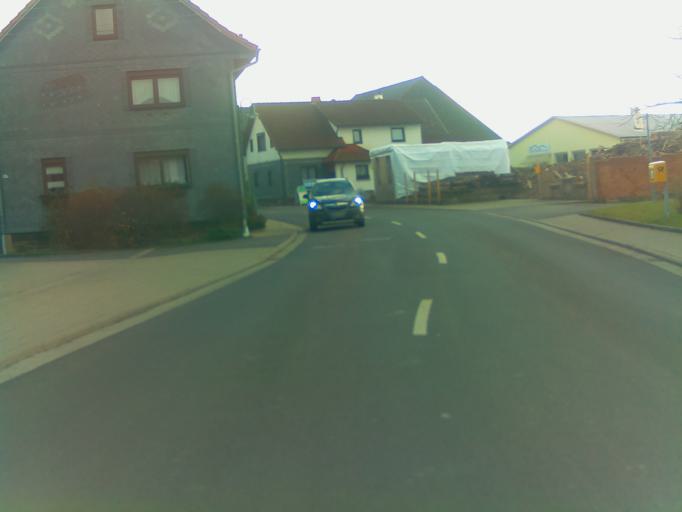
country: DE
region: Thuringia
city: Gleichamberg
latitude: 50.3882
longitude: 10.6532
